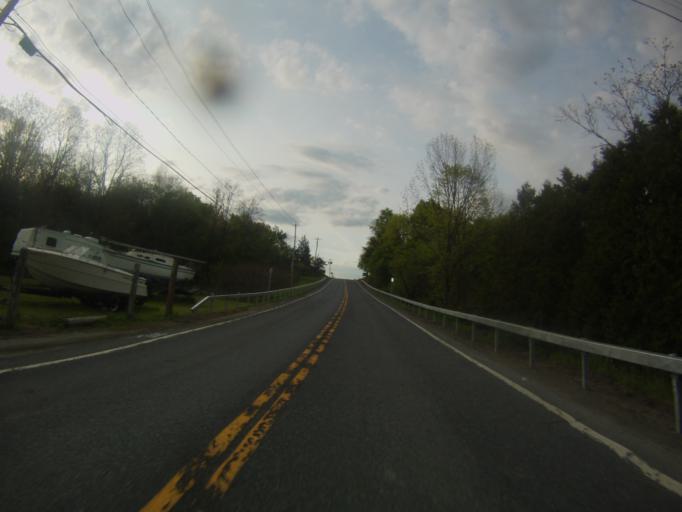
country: US
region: New York
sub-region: Essex County
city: Port Henry
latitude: 43.9600
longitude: -73.4301
